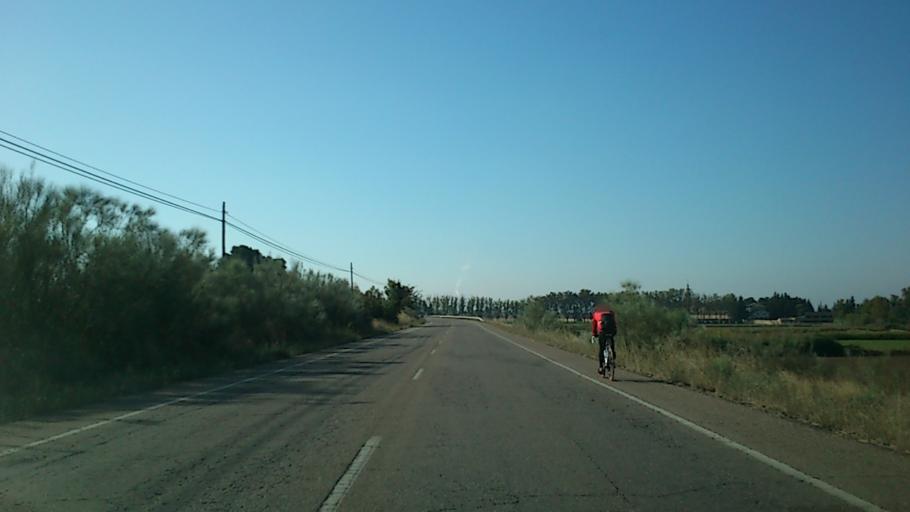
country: ES
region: Aragon
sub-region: Provincia de Zaragoza
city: Villanueva de Gallego
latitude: 41.7386
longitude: -0.8076
